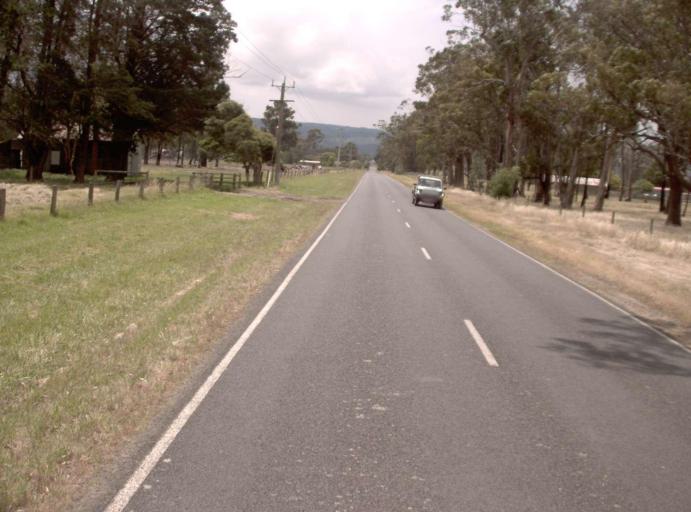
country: AU
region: Victoria
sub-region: Latrobe
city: Traralgon
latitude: -38.5341
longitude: 146.6580
